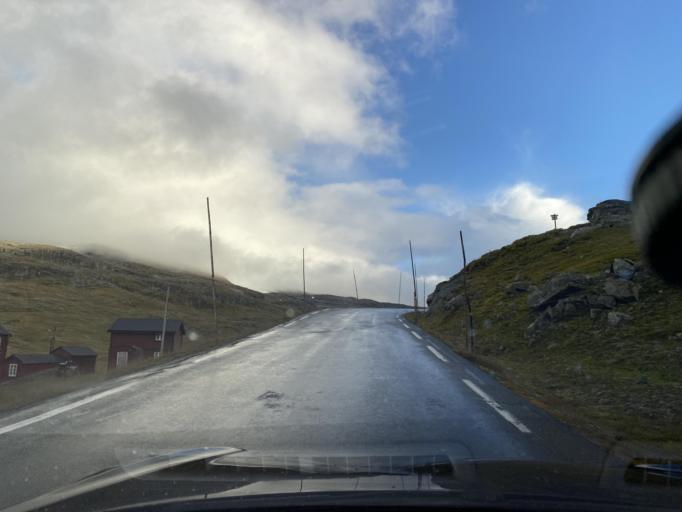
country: NO
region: Sogn og Fjordane
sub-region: Ardal
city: Farnes
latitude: 61.5743
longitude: 8.0311
